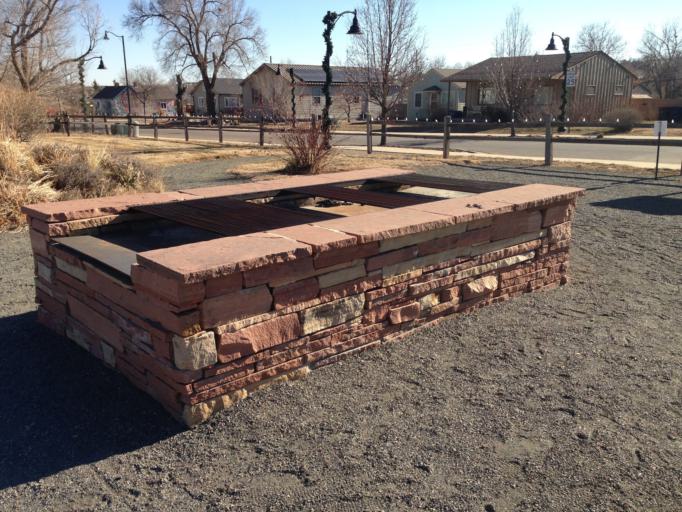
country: US
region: Colorado
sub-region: Boulder County
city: Superior
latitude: 39.9543
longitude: -105.1677
